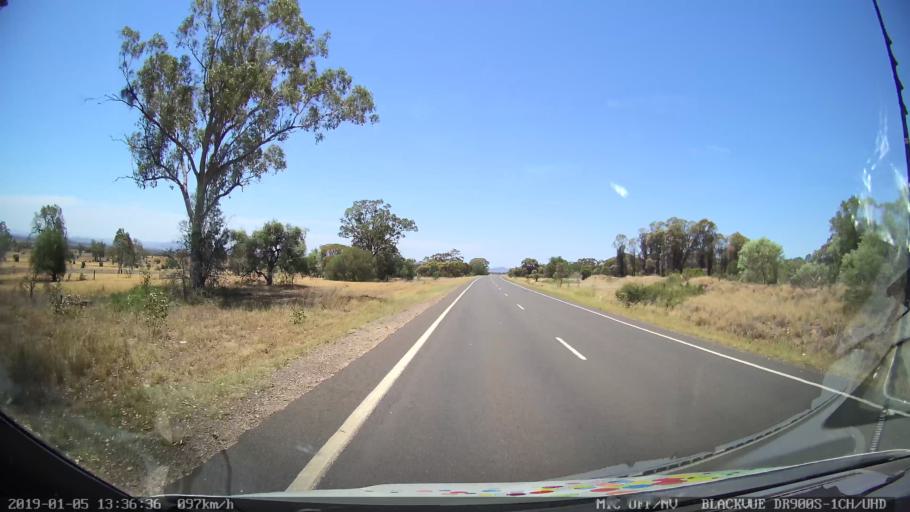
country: AU
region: New South Wales
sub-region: Gunnedah
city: Gunnedah
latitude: -30.9840
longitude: 150.1673
